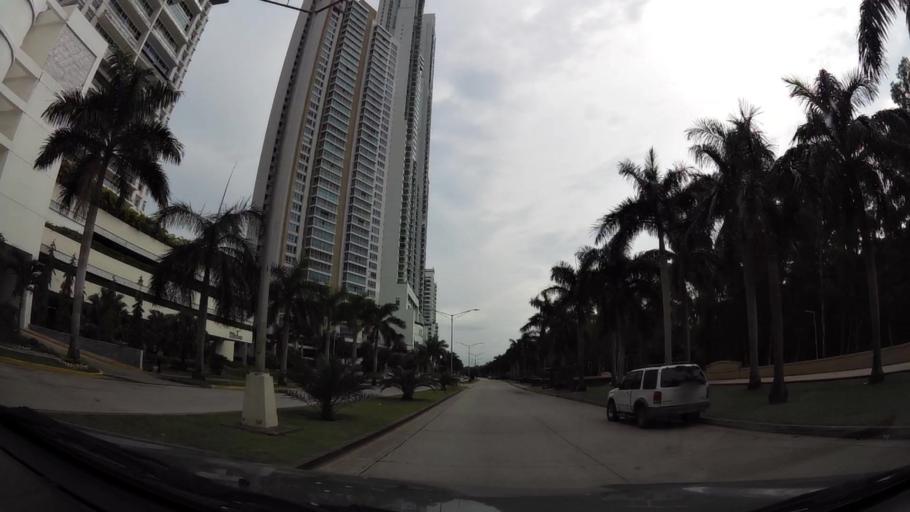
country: PA
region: Panama
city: San Miguelito
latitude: 9.0099
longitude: -79.4658
